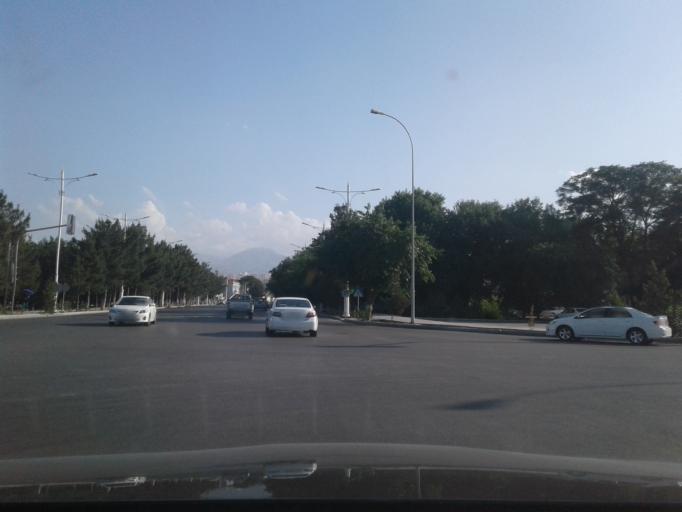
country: TM
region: Ahal
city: Ashgabat
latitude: 37.9604
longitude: 58.3603
